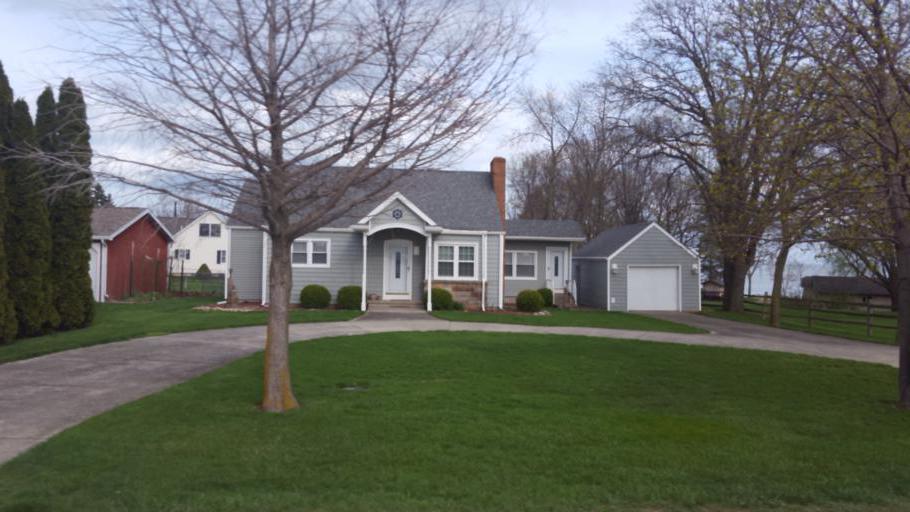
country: US
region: Ohio
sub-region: Erie County
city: Sandusky
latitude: 41.5217
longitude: -82.7206
